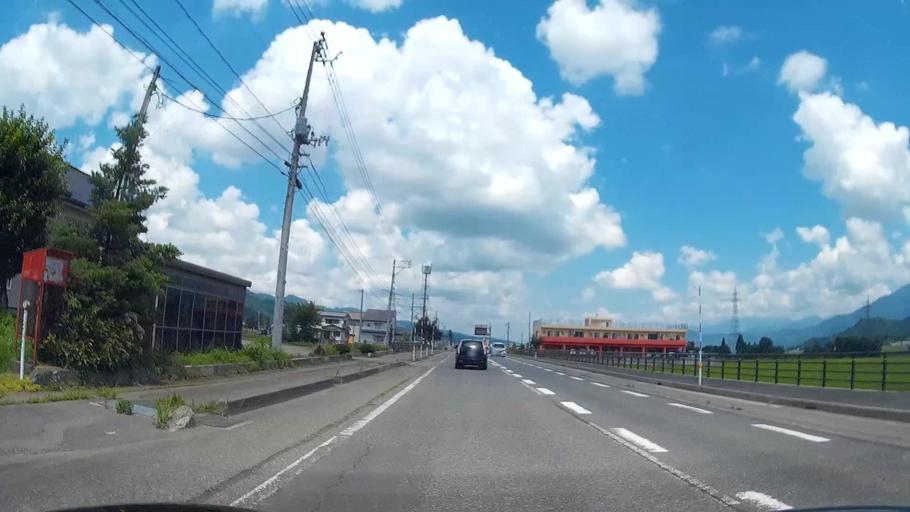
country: JP
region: Niigata
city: Shiozawa
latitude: 36.9905
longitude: 138.8102
